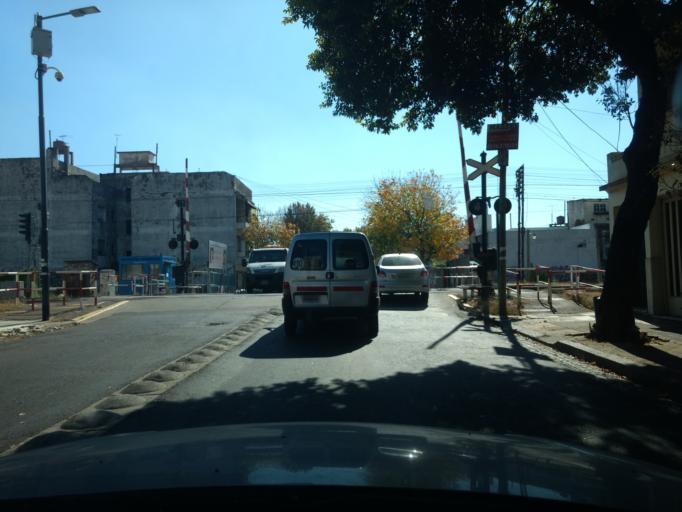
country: AR
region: Buenos Aires F.D.
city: Villa Santa Rita
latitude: -34.6352
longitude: -58.4924
